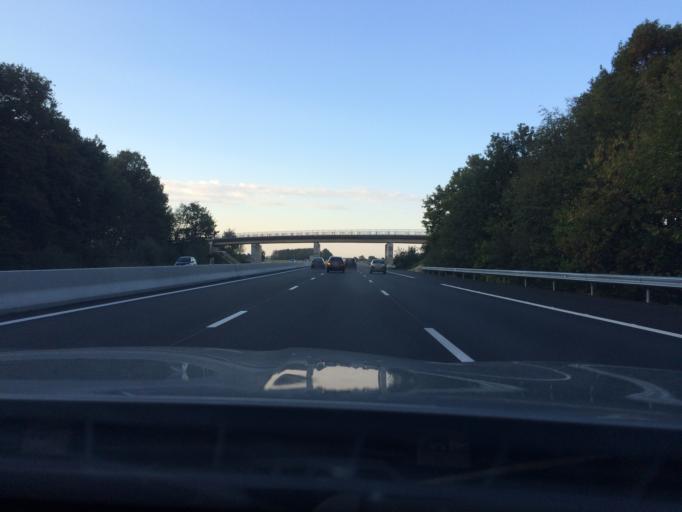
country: FR
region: Ile-de-France
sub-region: Departement de l'Essonne
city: Soisy-sur-Ecole
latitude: 48.5063
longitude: 2.5116
